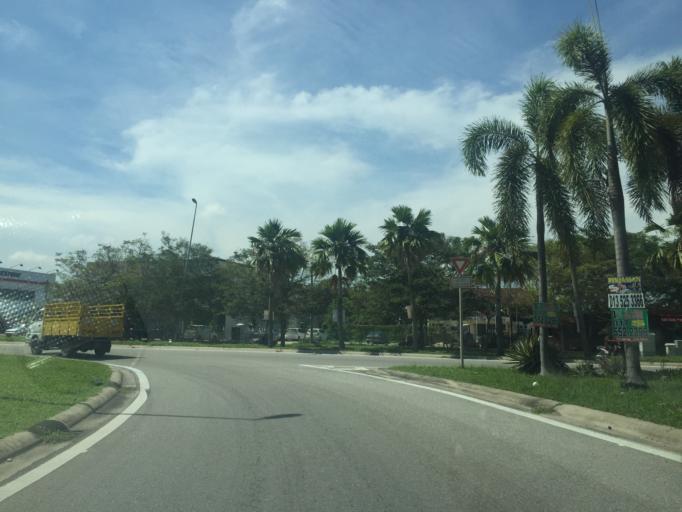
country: MY
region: Penang
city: Permatang Kuching
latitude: 5.4466
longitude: 100.3970
